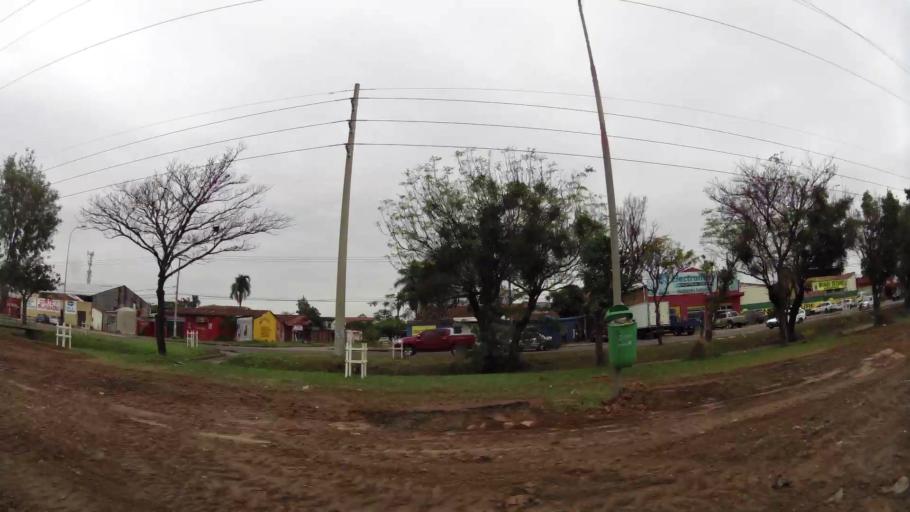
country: BO
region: Santa Cruz
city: Santa Cruz de la Sierra
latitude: -17.7705
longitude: -63.1470
